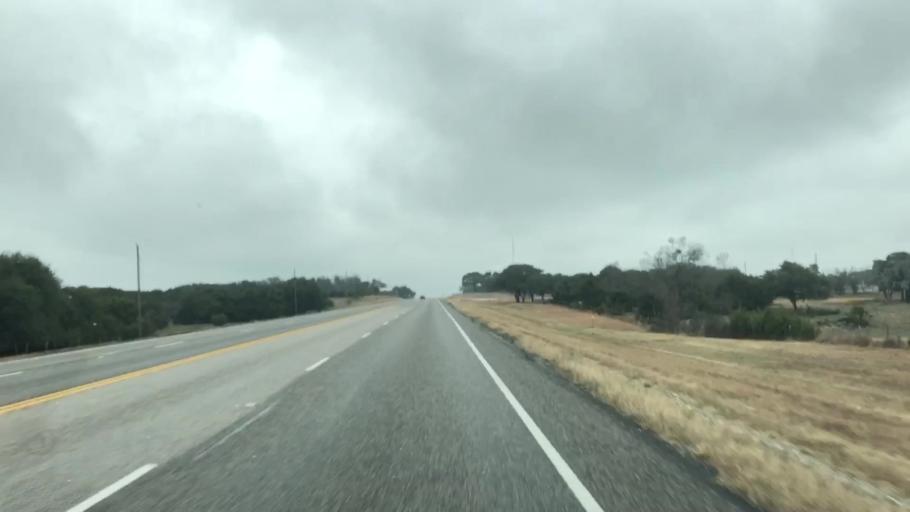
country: US
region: Texas
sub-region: Burnet County
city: Burnet
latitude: 30.8872
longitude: -98.2366
